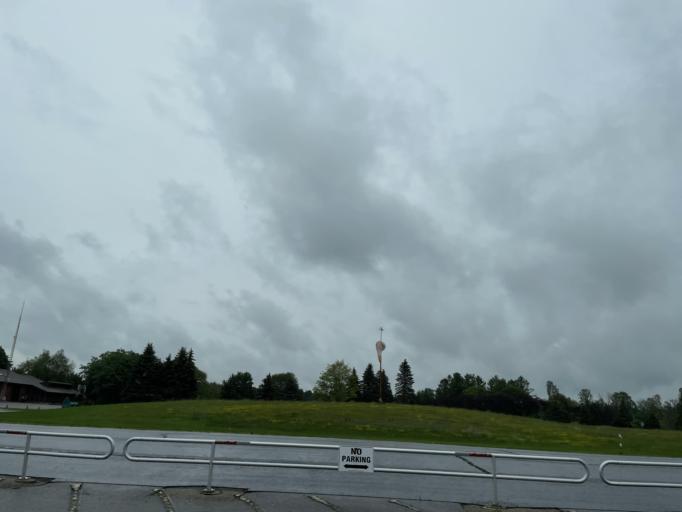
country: CA
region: Ontario
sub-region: Wellington County
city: Guelph
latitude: 43.4464
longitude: -80.2344
